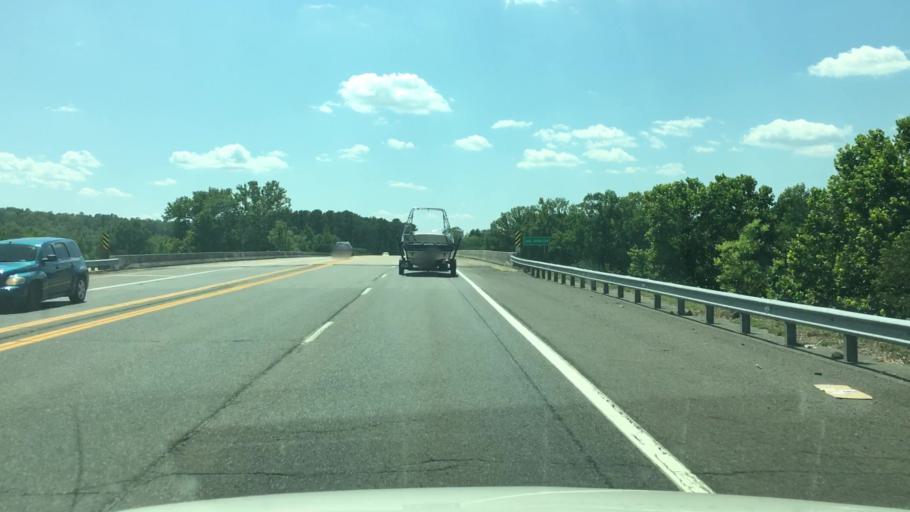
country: US
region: Arkansas
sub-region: Garland County
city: Piney
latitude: 34.5081
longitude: -93.1807
